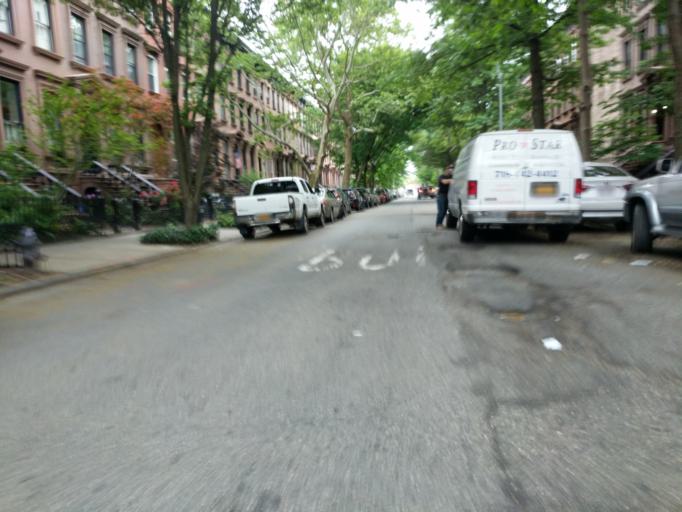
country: US
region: New York
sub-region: Kings County
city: Brooklyn
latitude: 40.6846
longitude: -73.9620
